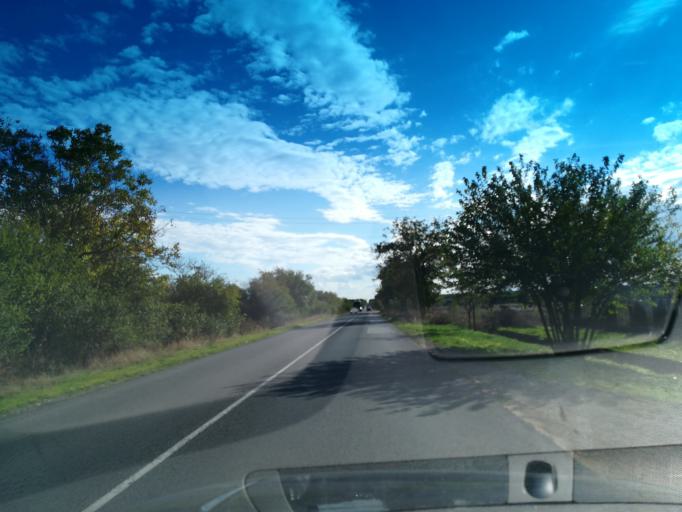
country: BG
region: Stara Zagora
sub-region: Obshtina Stara Zagora
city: Stara Zagora
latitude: 42.3672
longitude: 25.6541
